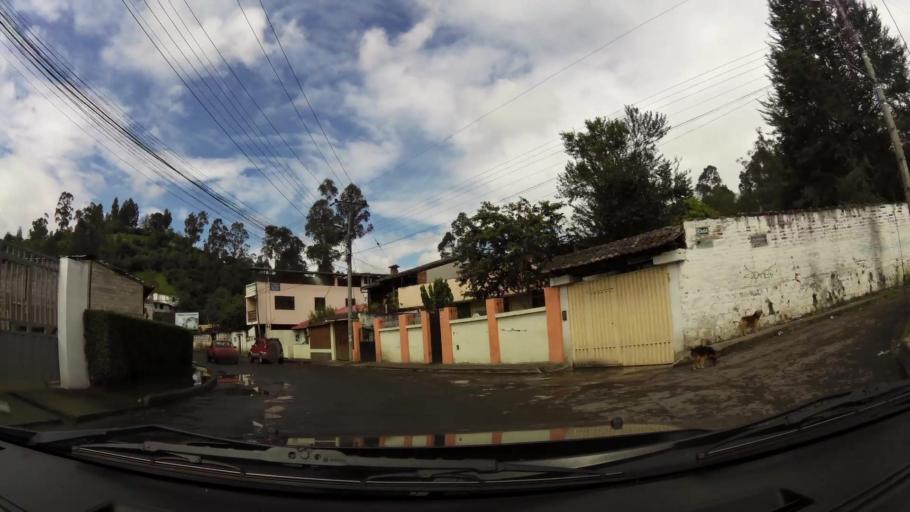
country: EC
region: Pichincha
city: Sangolqui
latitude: -0.3040
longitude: -78.4308
